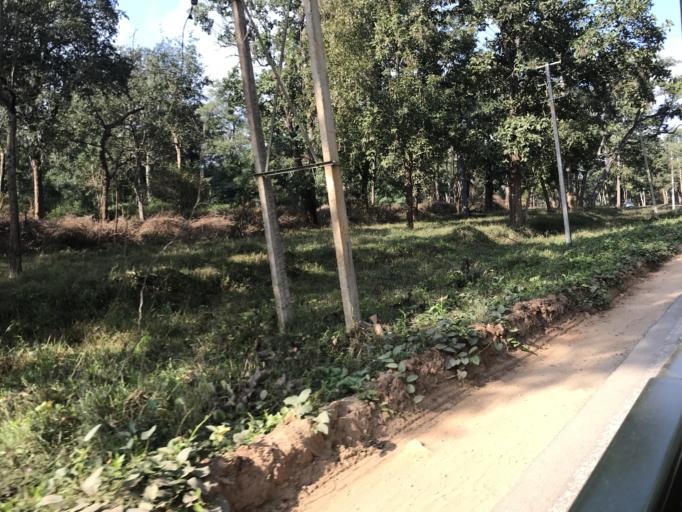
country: IN
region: Karnataka
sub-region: Mysore
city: Heggadadevankote
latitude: 11.9429
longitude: 76.2138
